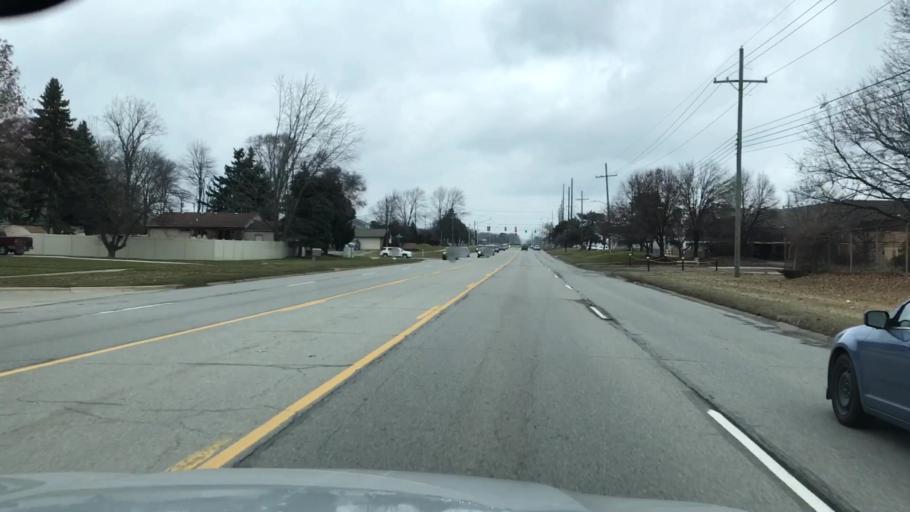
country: US
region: Michigan
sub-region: Wayne County
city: Westland
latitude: 42.3721
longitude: -83.4115
